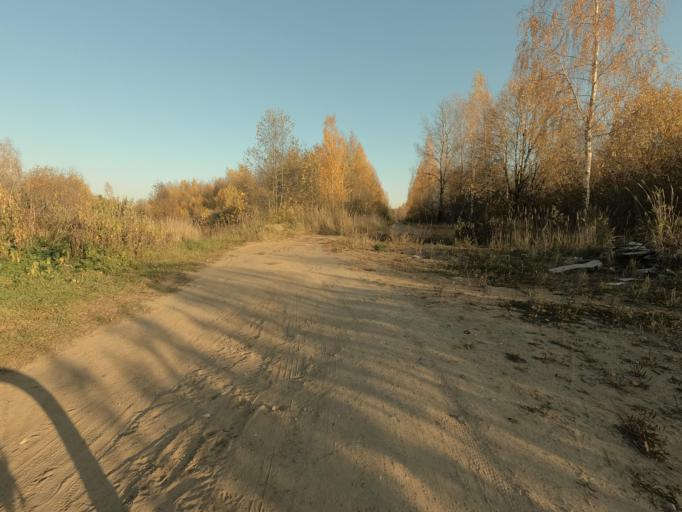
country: RU
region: Leningrad
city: Kirovsk
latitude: 59.8644
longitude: 31.0127
